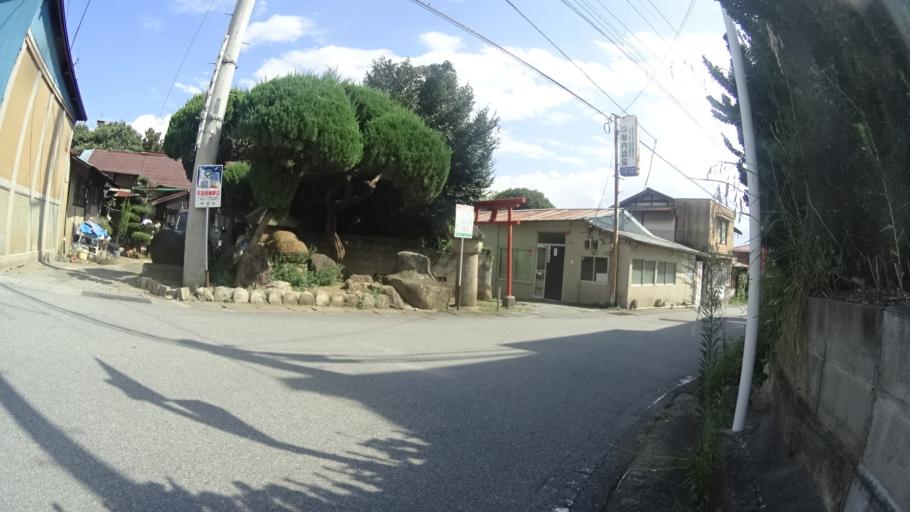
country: JP
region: Yamanashi
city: Enzan
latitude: 35.7086
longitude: 138.7318
